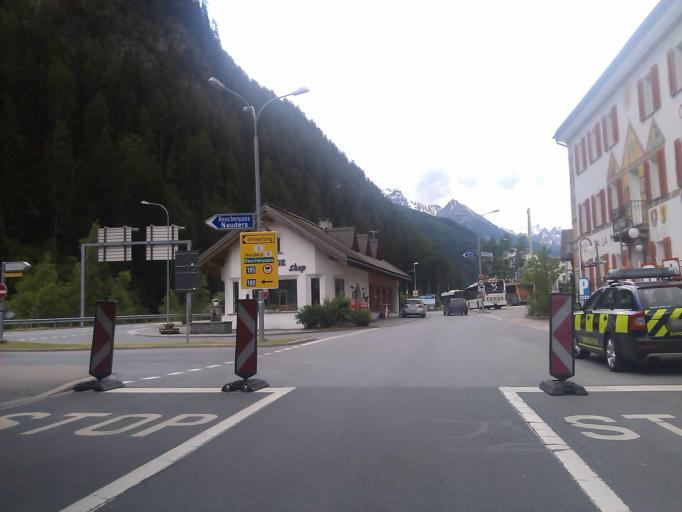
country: AT
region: Tyrol
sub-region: Politischer Bezirk Landeck
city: Nauders
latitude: 46.8851
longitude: 10.4644
